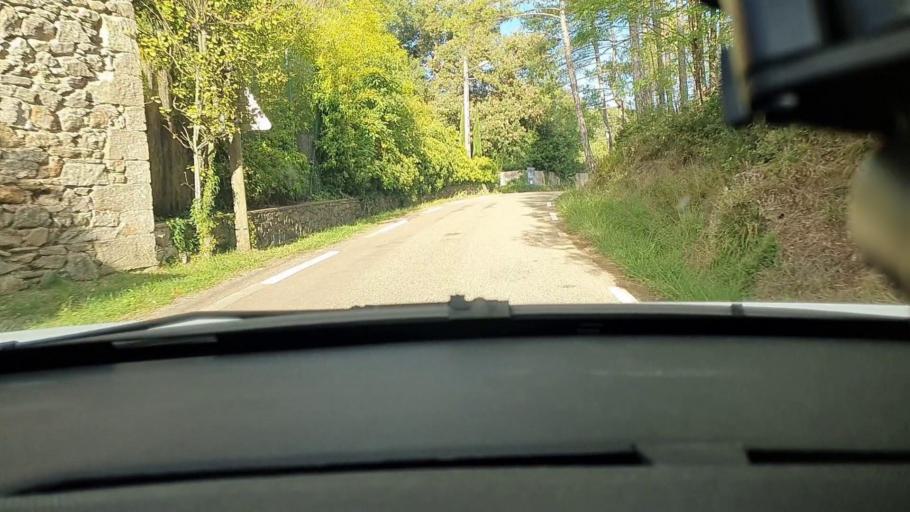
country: FR
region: Languedoc-Roussillon
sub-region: Departement du Gard
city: Besseges
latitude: 44.3223
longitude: 4.1206
